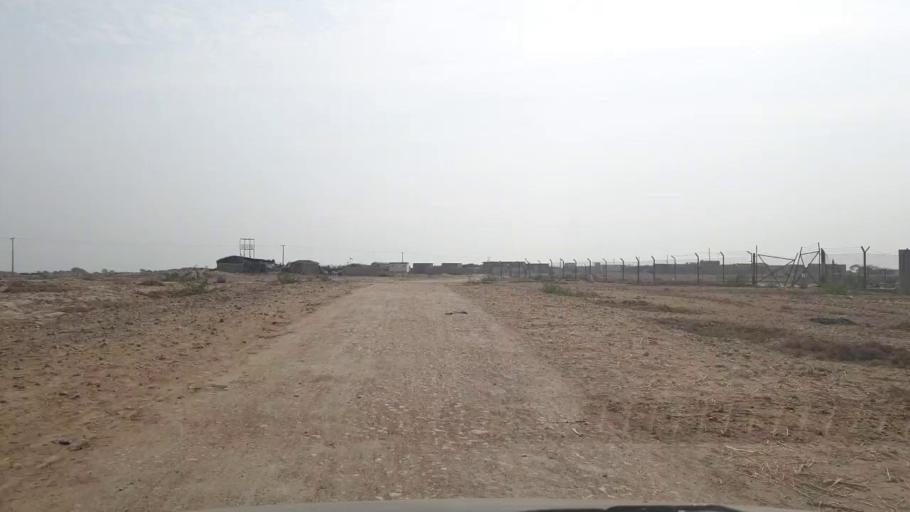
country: PK
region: Sindh
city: Tando Muhammad Khan
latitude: 25.1601
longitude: 68.4697
